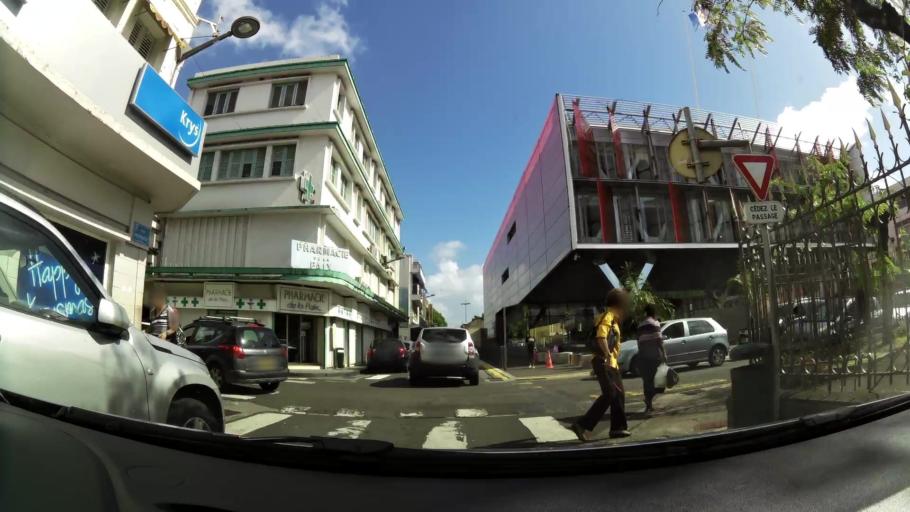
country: MQ
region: Martinique
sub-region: Martinique
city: Fort-de-France
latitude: 14.6052
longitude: -61.0691
